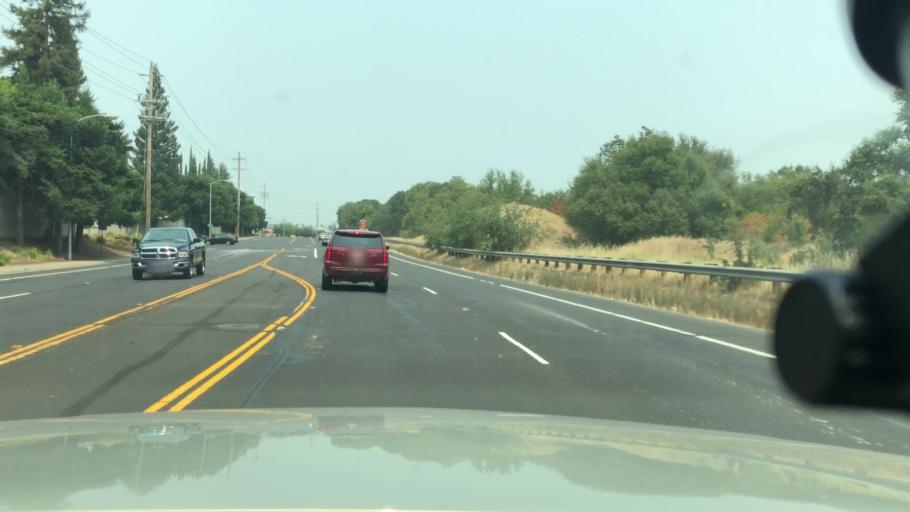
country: US
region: California
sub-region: Sacramento County
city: Folsom
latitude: 38.6652
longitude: -121.1561
